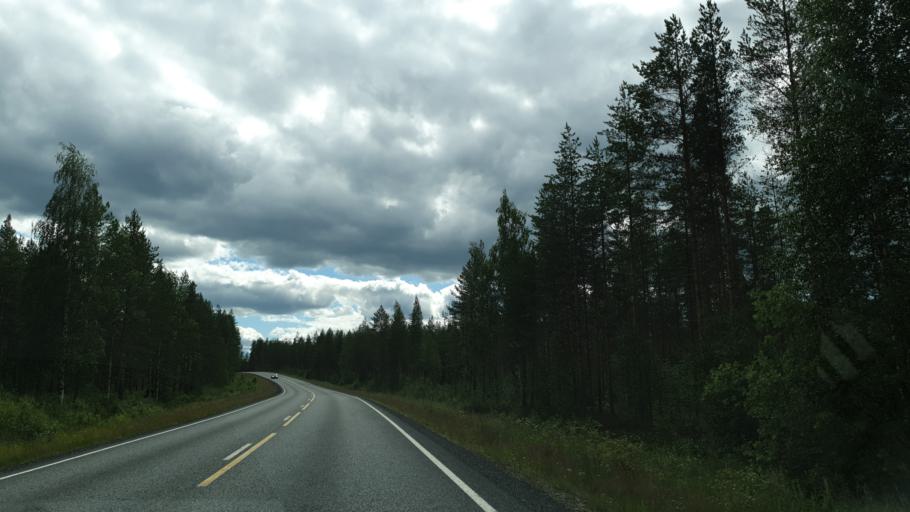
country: FI
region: Kainuu
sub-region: Kehys-Kainuu
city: Kuhmo
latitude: 64.0565
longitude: 29.5392
